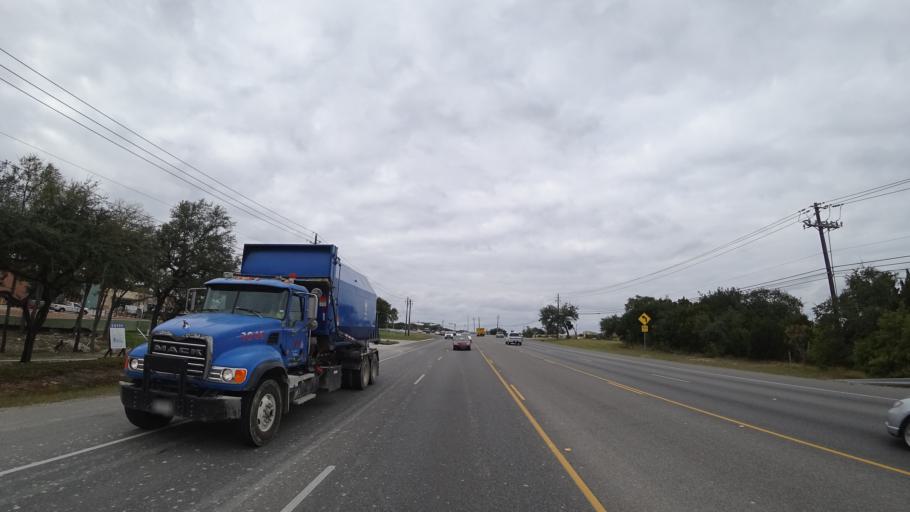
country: US
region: Texas
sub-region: Travis County
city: Bee Cave
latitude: 30.3233
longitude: -97.9566
